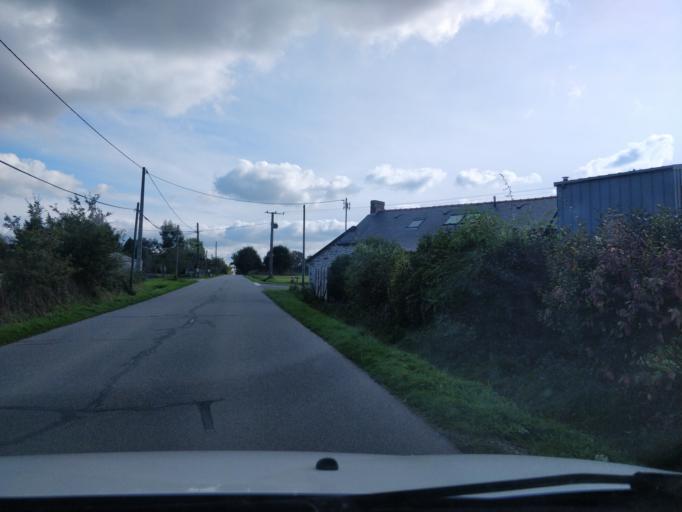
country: FR
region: Brittany
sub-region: Departement d'Ille-et-Vilaine
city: La Bouexiere
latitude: 48.1702
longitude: -1.4291
